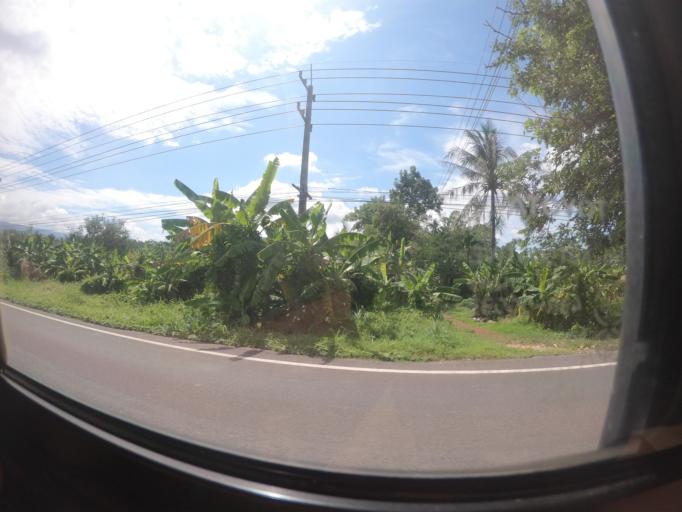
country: TH
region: Nakhon Nayok
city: Nakhon Nayok
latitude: 14.2899
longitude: 101.3032
